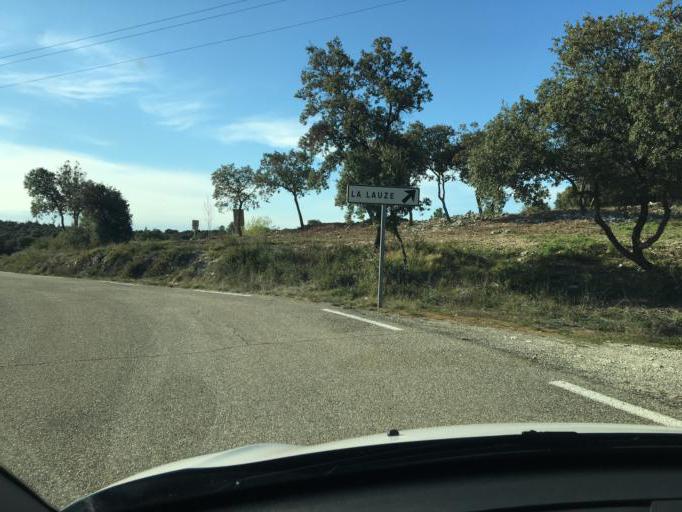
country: FR
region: Provence-Alpes-Cote d'Azur
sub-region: Departement du Vaucluse
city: Villes-sur-Auzon
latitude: 44.0420
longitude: 5.2562
